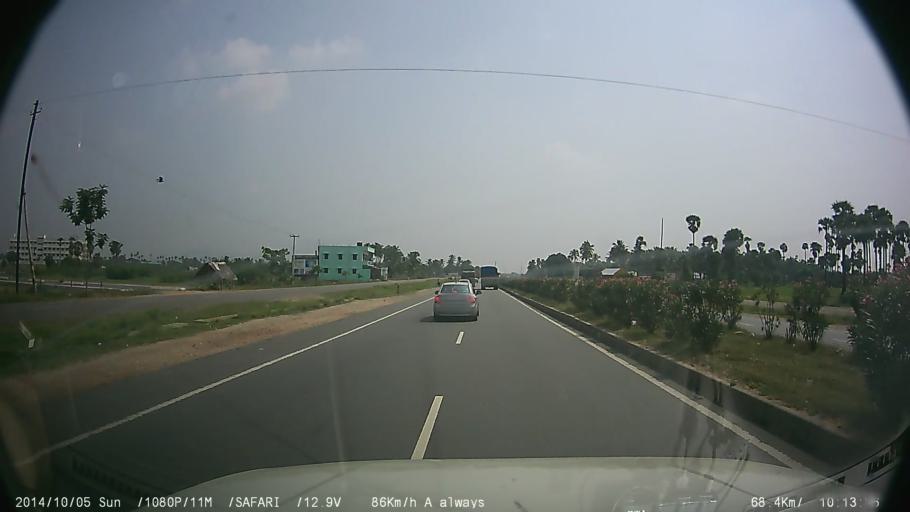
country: IN
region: Tamil Nadu
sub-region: Salem
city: Ilampillai
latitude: 11.5503
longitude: 77.9981
